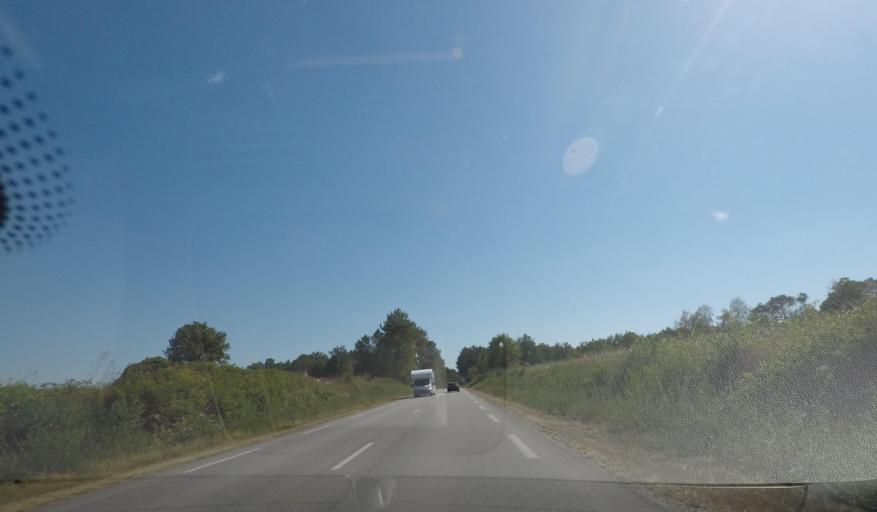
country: FR
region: Brittany
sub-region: Departement du Morbihan
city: Peaule
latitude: 47.5817
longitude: -2.3777
